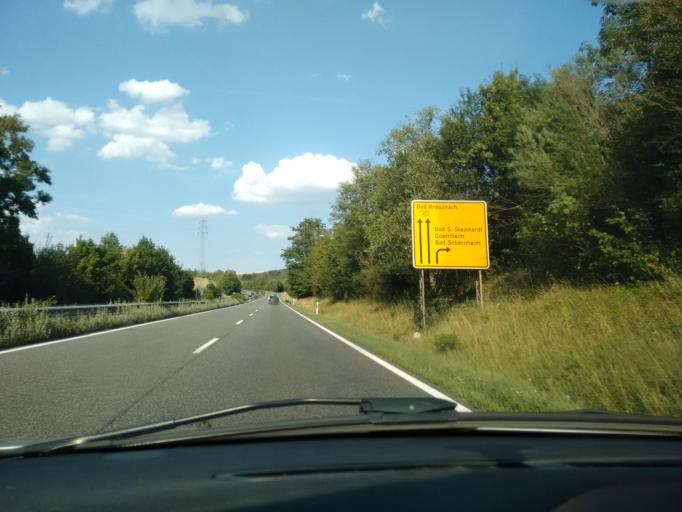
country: DE
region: Rheinland-Pfalz
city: Staudernheim
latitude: 49.7946
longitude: 7.6554
